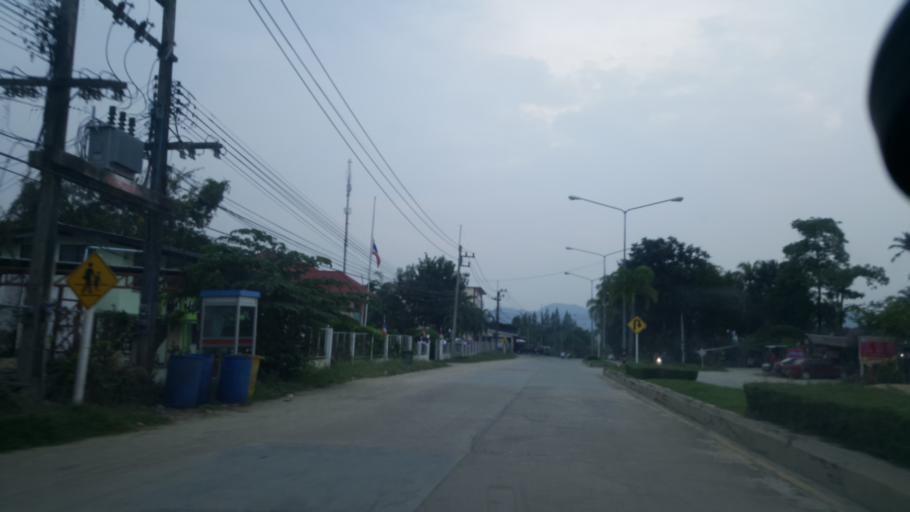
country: TH
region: Chon Buri
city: Si Racha
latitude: 13.2373
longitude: 101.0064
